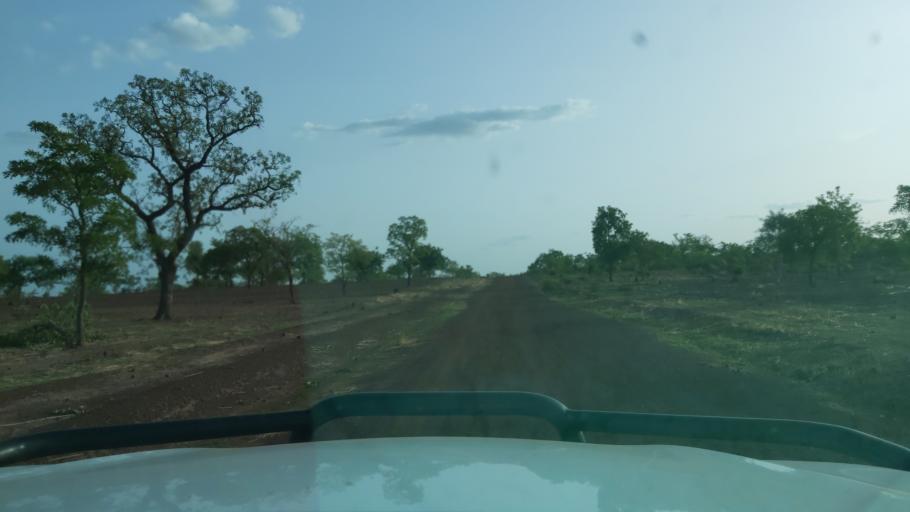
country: ML
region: Koulikoro
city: Kolokani
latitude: 13.2119
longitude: -7.9020
